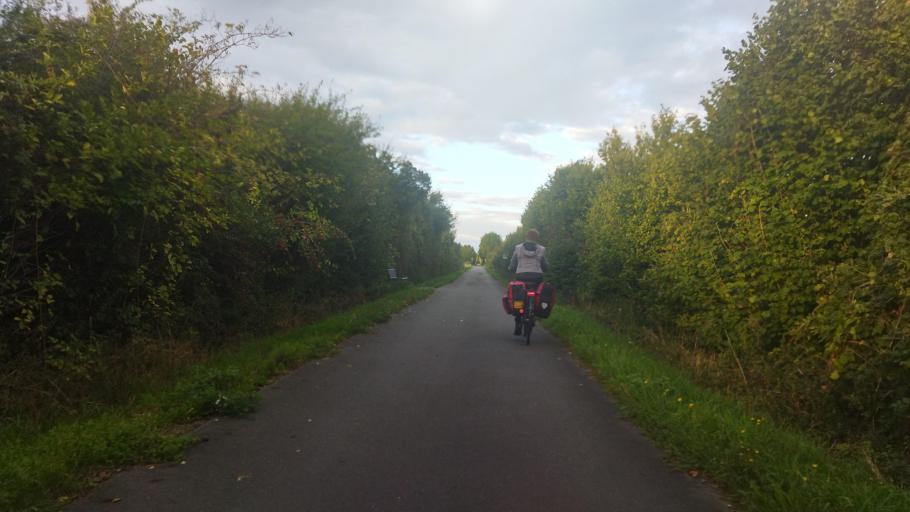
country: DE
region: North Rhine-Westphalia
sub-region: Regierungsbezirk Munster
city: Billerbeck
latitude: 51.9999
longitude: 7.2461
